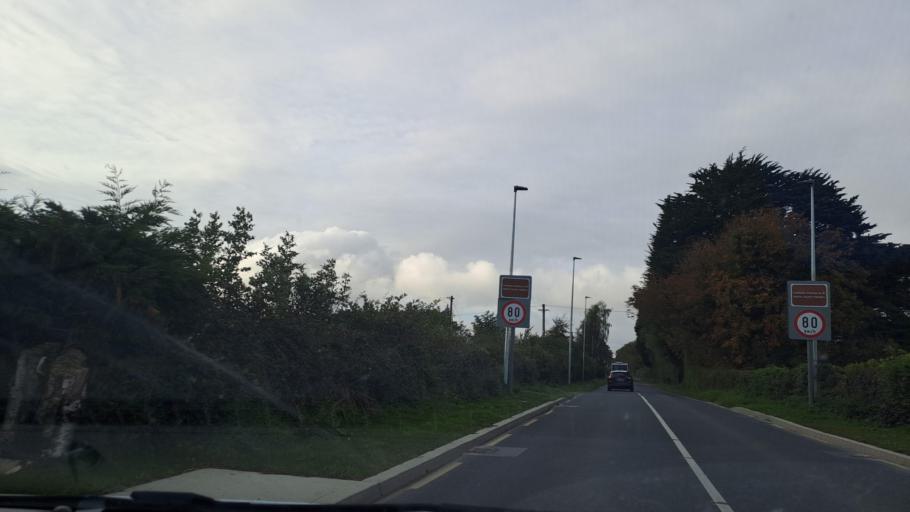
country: IE
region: Leinster
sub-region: An Mhi
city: Navan
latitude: 53.7078
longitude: -6.6870
